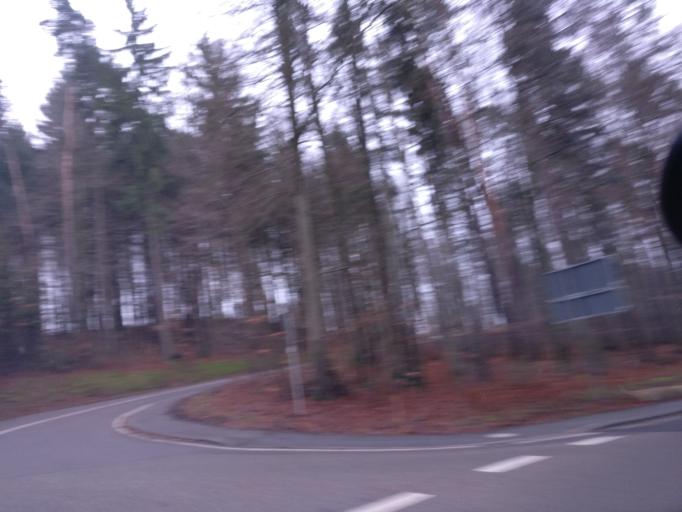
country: DE
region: Baden-Wuerttemberg
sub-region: Regierungsbezirk Stuttgart
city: Rudersberg
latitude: 48.8502
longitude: 9.4929
